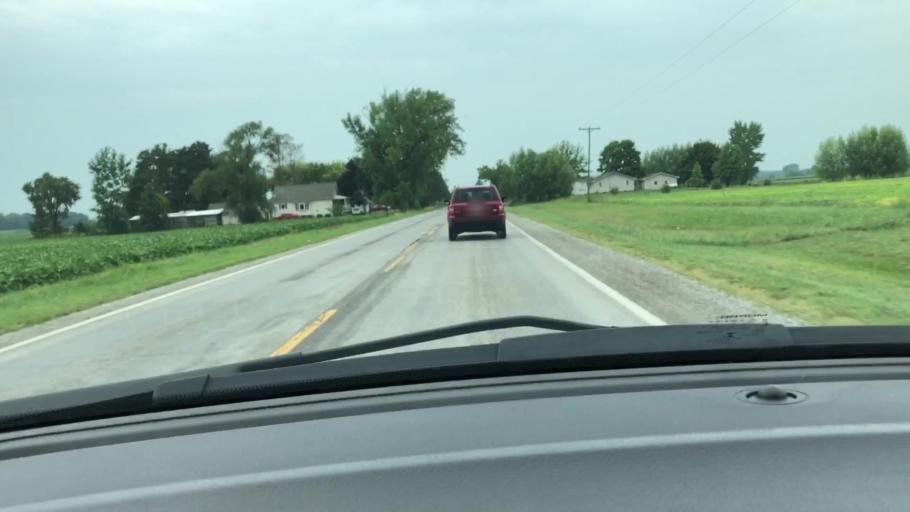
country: US
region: Michigan
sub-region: Saginaw County
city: Freeland
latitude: 43.5486
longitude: -84.0901
